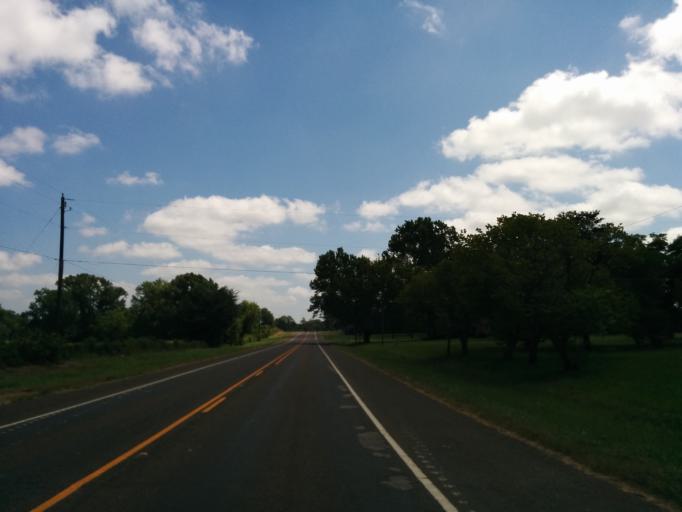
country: US
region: Texas
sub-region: Houston County
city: Crockett
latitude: 31.3321
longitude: -95.4317
